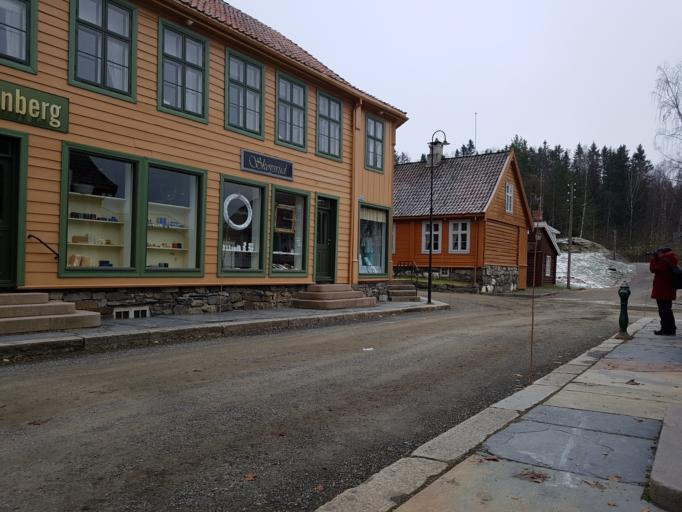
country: NO
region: Oppland
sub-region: Lillehammer
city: Lillehammer
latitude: 61.1127
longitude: 10.4786
